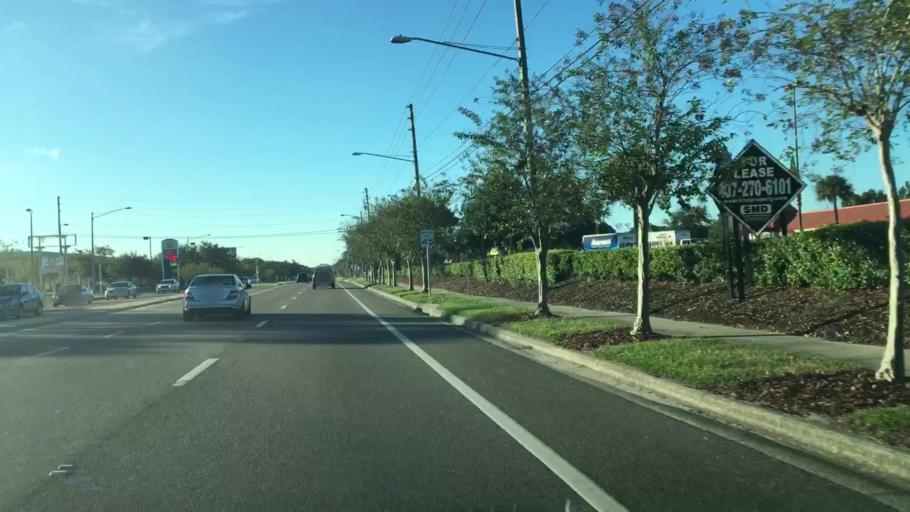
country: US
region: Florida
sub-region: Orange County
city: Azalea Park
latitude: 28.5364
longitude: -81.2859
